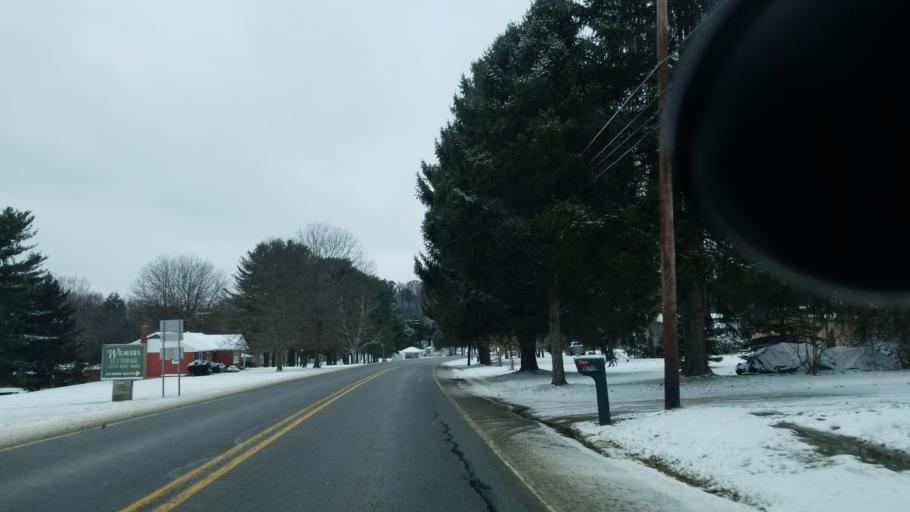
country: US
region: Pennsylvania
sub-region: Jefferson County
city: Albion
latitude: 40.9320
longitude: -78.9079
